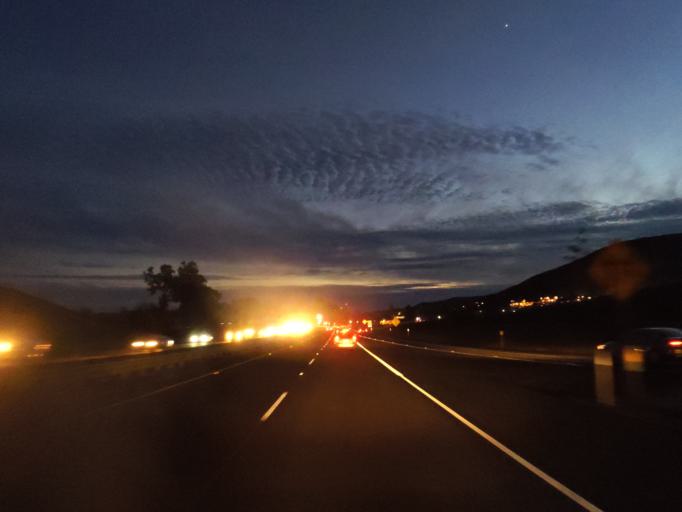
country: US
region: California
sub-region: San Luis Obispo County
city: San Luis Obispo
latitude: 35.2724
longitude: -120.6722
